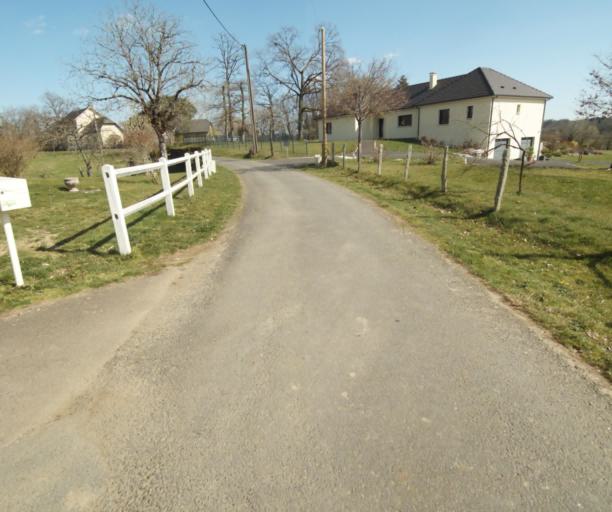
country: FR
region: Limousin
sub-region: Departement de la Correze
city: Saint-Mexant
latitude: 45.3060
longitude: 1.6492
